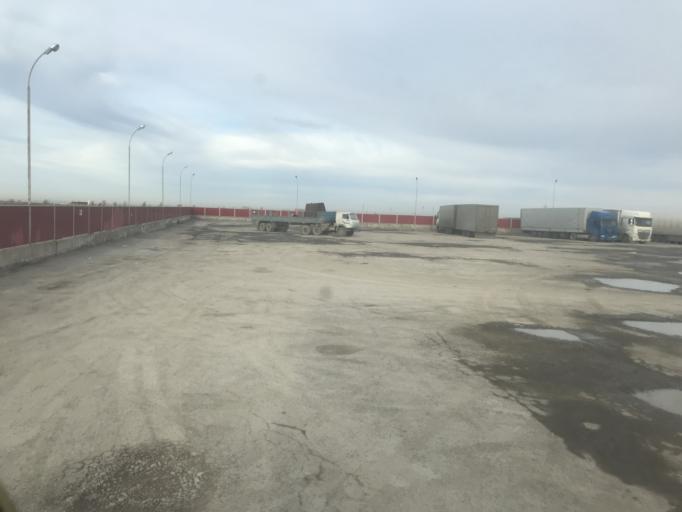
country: KZ
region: Ongtustik Qazaqstan
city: Shymkent
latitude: 42.4618
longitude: 69.5747
